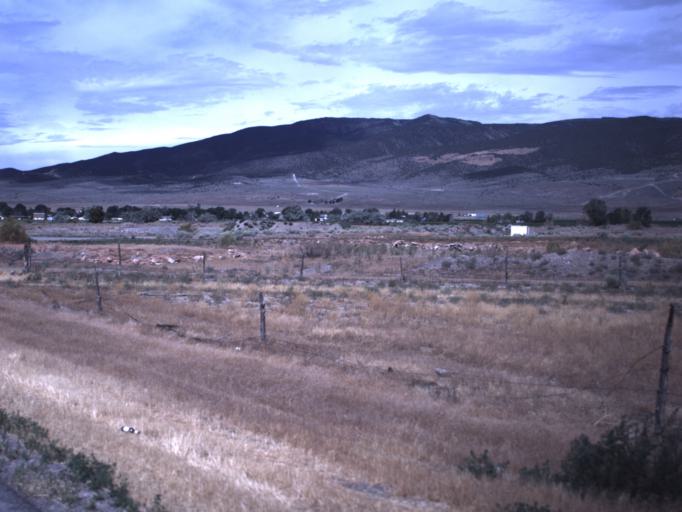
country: US
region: Utah
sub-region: Sevier County
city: Monroe
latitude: 38.6276
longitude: -112.1997
